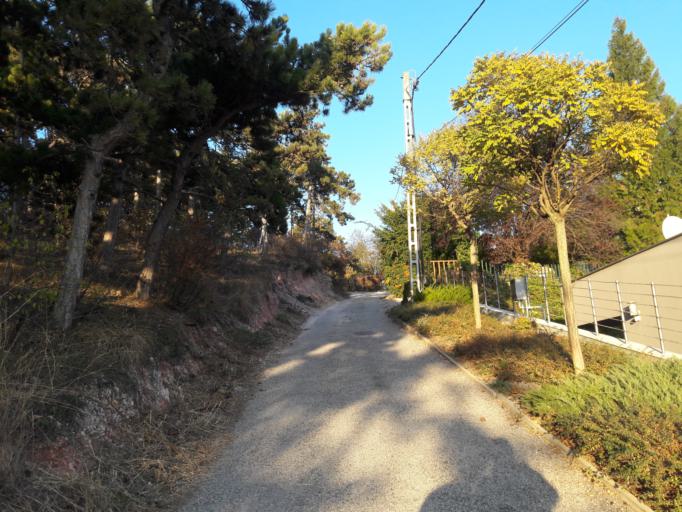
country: HU
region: Pest
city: Budaors
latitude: 47.4692
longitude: 18.9654
